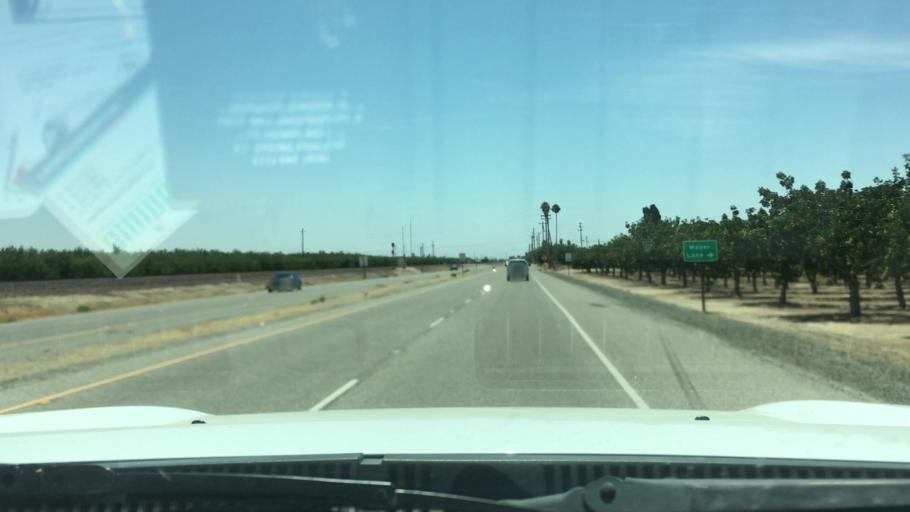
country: US
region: California
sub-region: Kern County
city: Shafter
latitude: 35.5181
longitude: -119.2928
